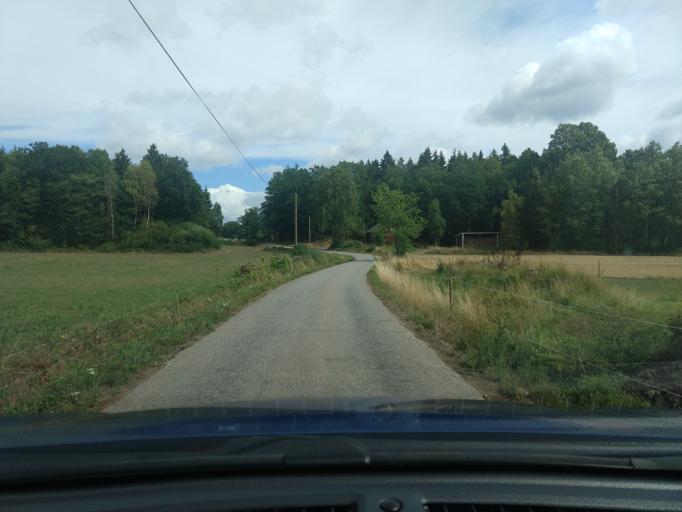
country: SE
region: Blekinge
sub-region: Ronneby Kommun
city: Brakne-Hoby
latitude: 56.2897
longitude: 15.1929
